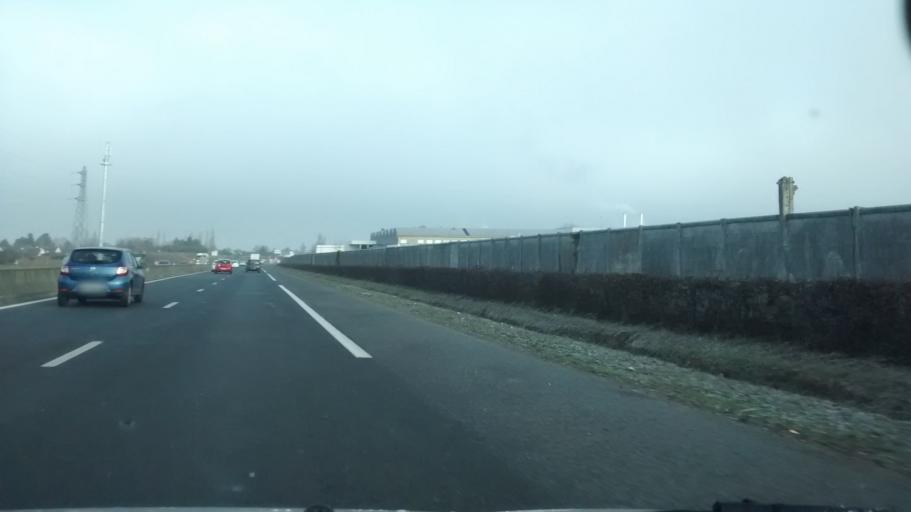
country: FR
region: Centre
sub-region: Departement d'Indre-et-Loire
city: Joue-les-Tours
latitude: 47.3535
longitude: 0.6460
